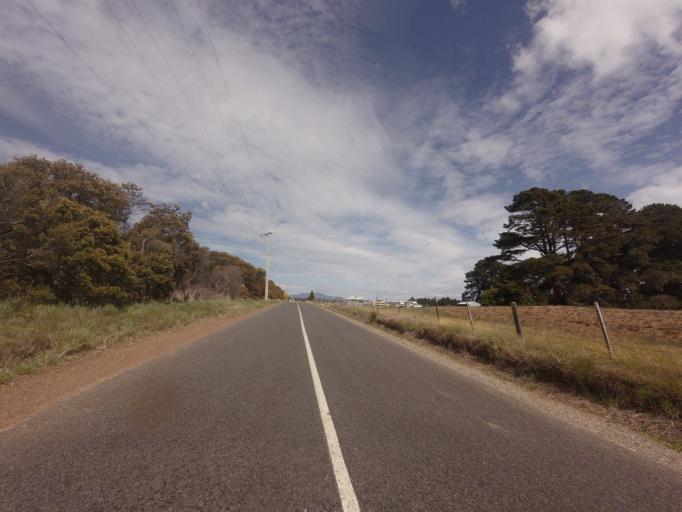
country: AU
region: Tasmania
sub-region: Northern Midlands
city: Longford
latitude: -41.6955
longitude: 147.1967
